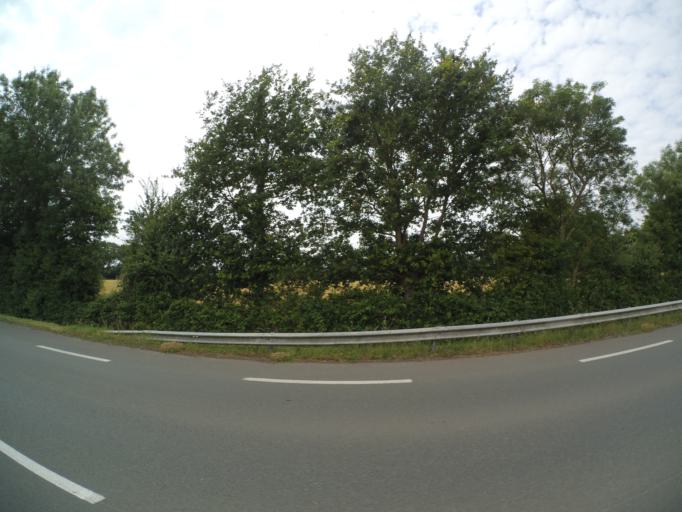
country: FR
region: Pays de la Loire
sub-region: Departement de la Vendee
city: Saint-Georges-de-Montaigu
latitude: 46.9286
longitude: -1.2615
